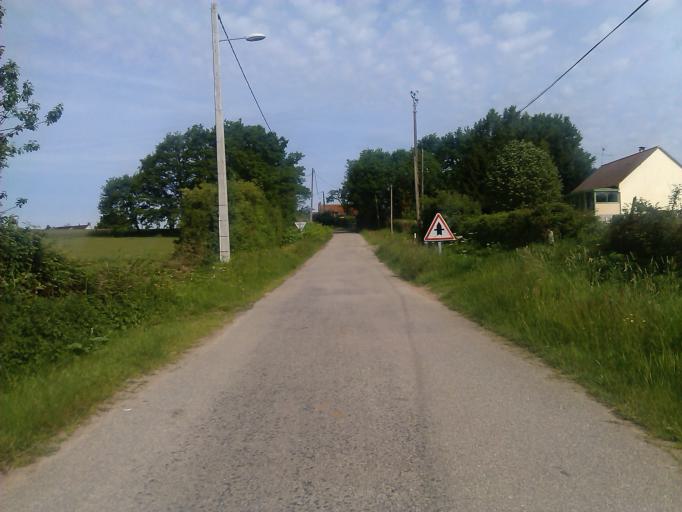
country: FR
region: Auvergne
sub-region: Departement de l'Allier
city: Vallon-en-Sully
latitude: 46.6131
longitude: 2.6572
